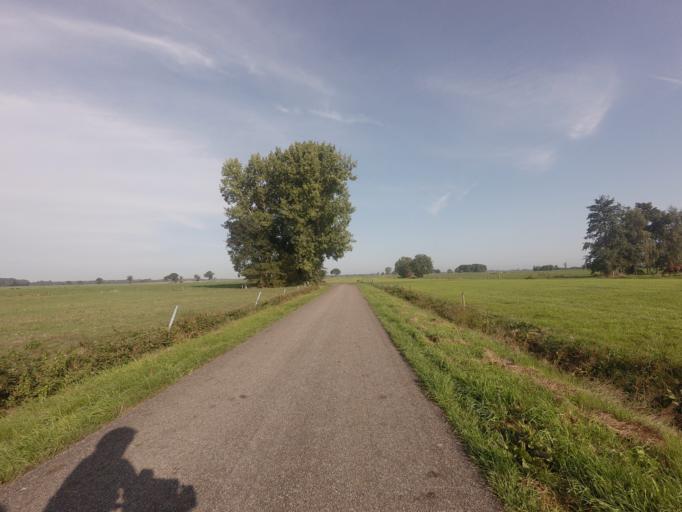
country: NL
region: Groningen
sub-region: Gemeente Leek
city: Leek
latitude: 53.1591
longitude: 6.4328
